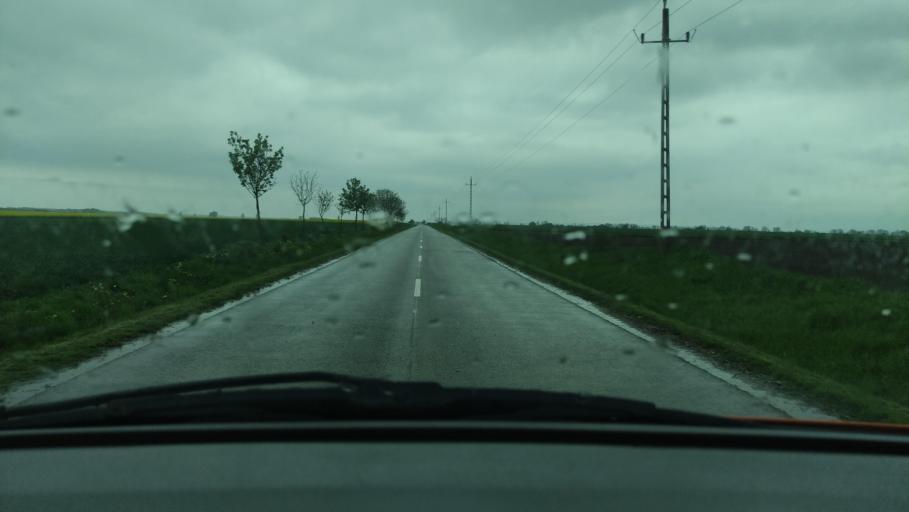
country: HU
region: Baranya
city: Mohacs
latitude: 45.9488
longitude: 18.6873
